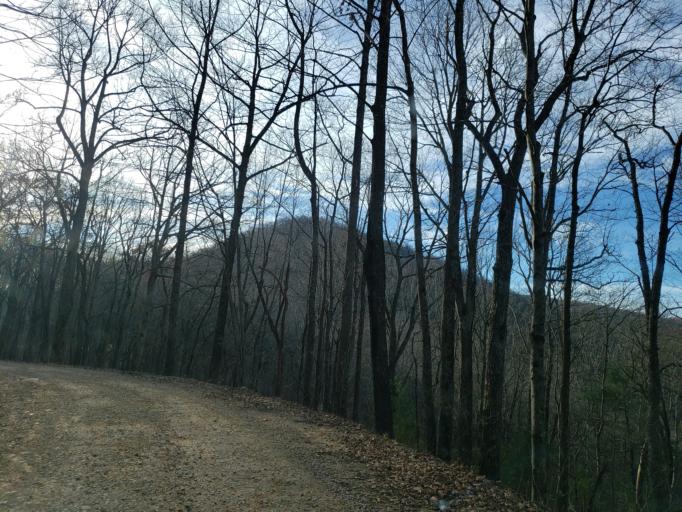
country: US
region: Georgia
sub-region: Lumpkin County
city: Dahlonega
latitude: 34.6565
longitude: -84.1033
